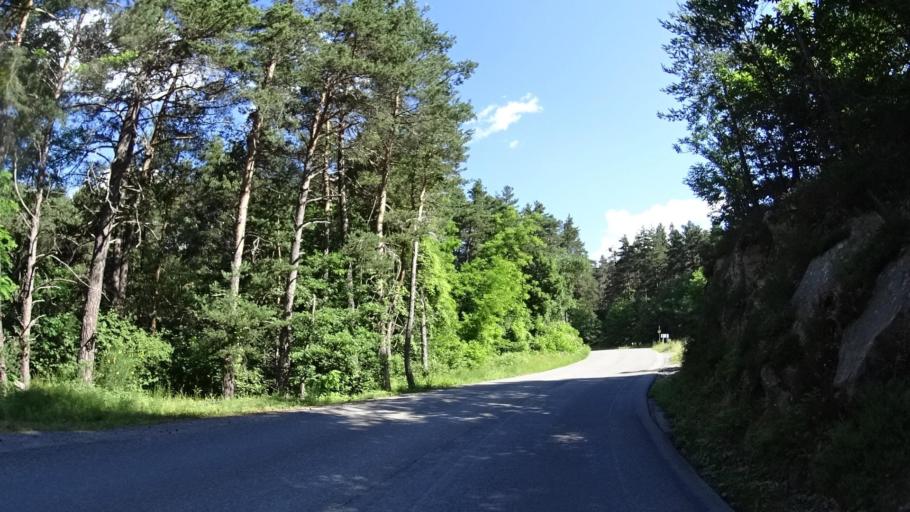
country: FR
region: Provence-Alpes-Cote d'Azur
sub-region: Departement des Alpes-de-Haute-Provence
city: Annot
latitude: 43.9813
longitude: 6.6500
